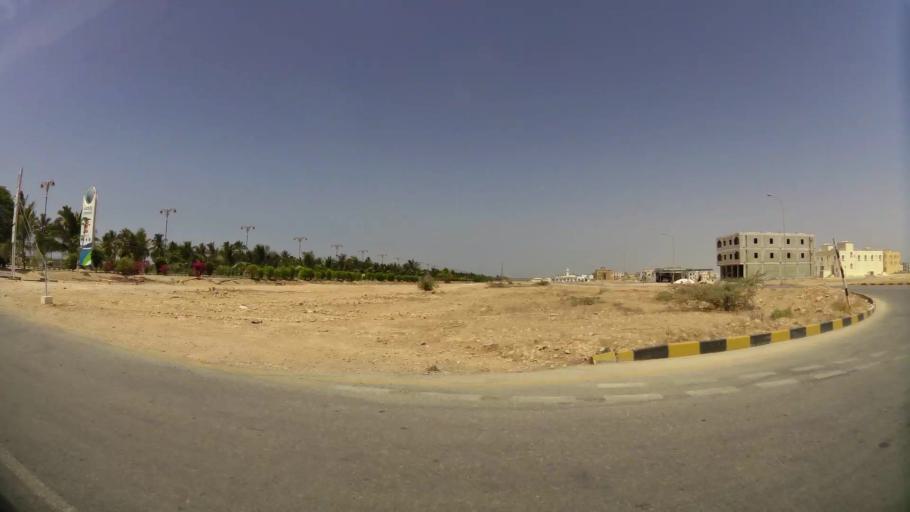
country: OM
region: Zufar
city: Salalah
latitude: 17.0488
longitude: 54.2134
